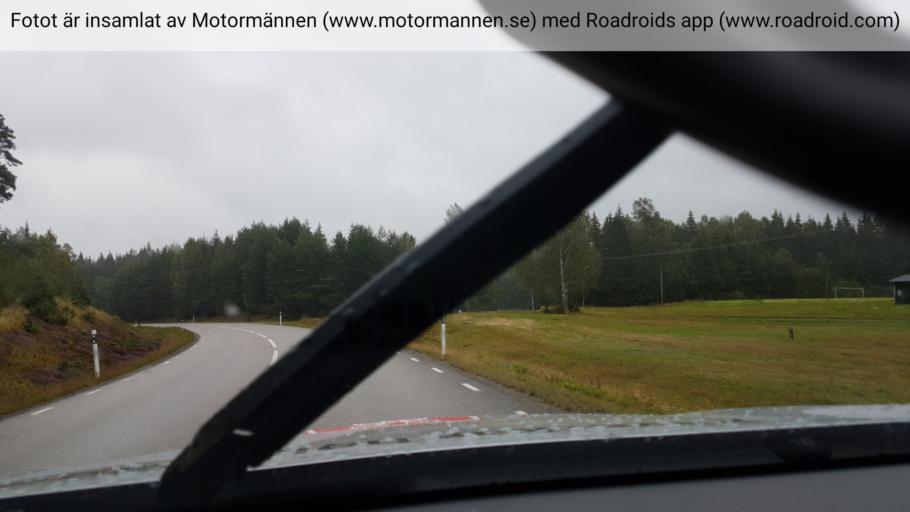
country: SE
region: Vaestra Goetaland
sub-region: Bengtsfors Kommun
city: Dals Langed
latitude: 58.8577
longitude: 12.1814
